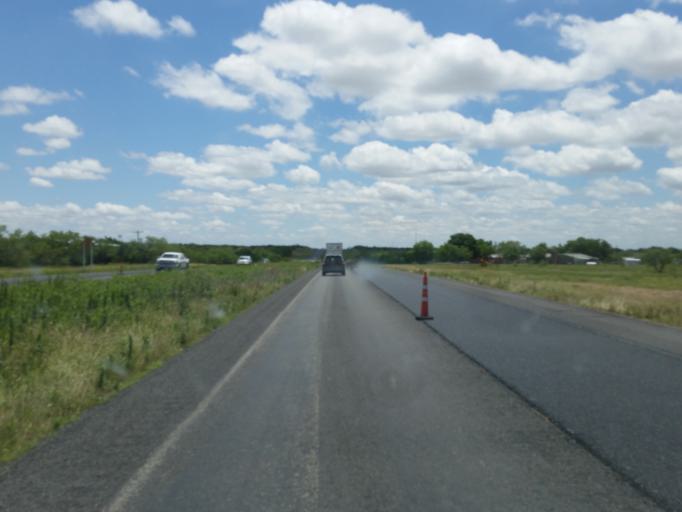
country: US
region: Texas
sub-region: Scurry County
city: Snyder
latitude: 32.7659
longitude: -100.9353
